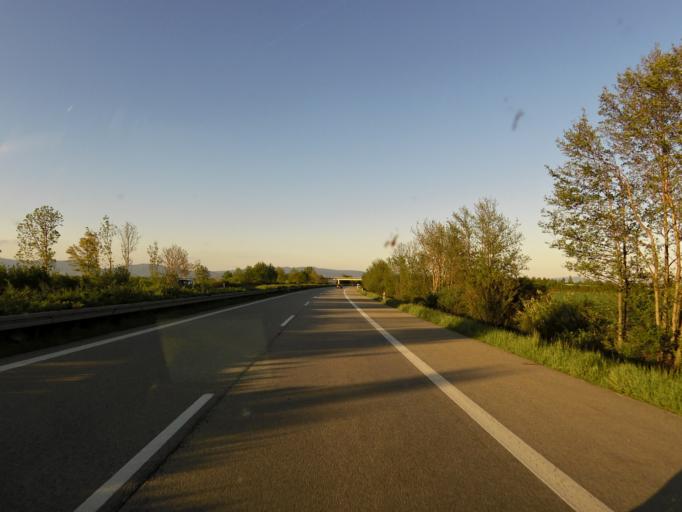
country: DE
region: Bavaria
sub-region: Lower Bavaria
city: Otzing
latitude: 48.7739
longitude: 12.7874
